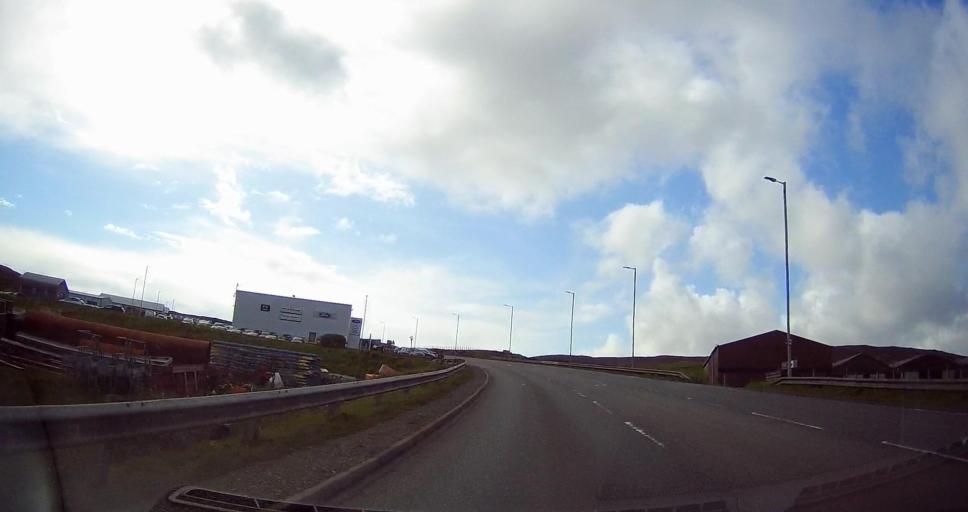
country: GB
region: Scotland
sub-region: Shetland Islands
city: Lerwick
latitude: 60.1700
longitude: -1.1687
